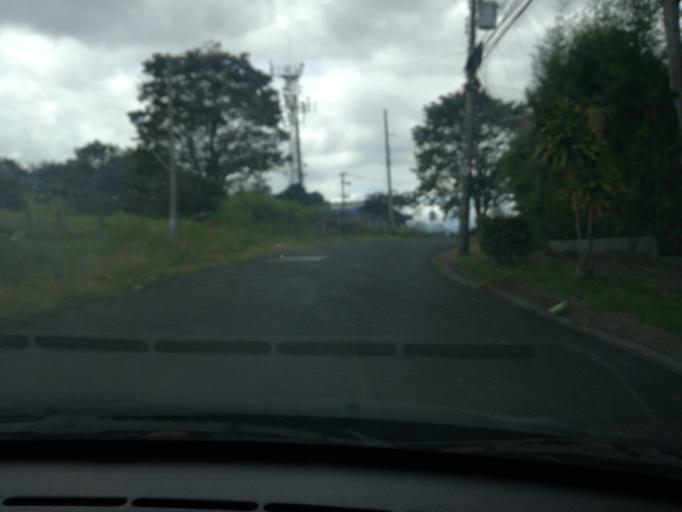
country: CR
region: San Jose
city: Curridabat
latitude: 9.9105
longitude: -84.0303
